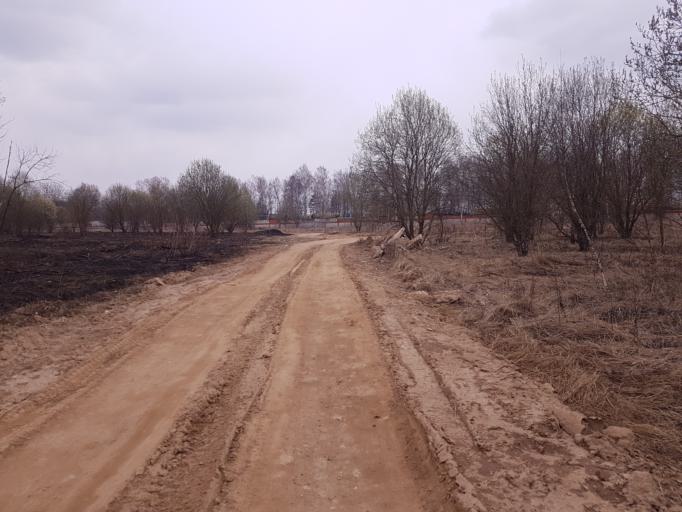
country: RU
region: Moskovskaya
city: Istra
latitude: 55.9039
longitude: 36.8729
